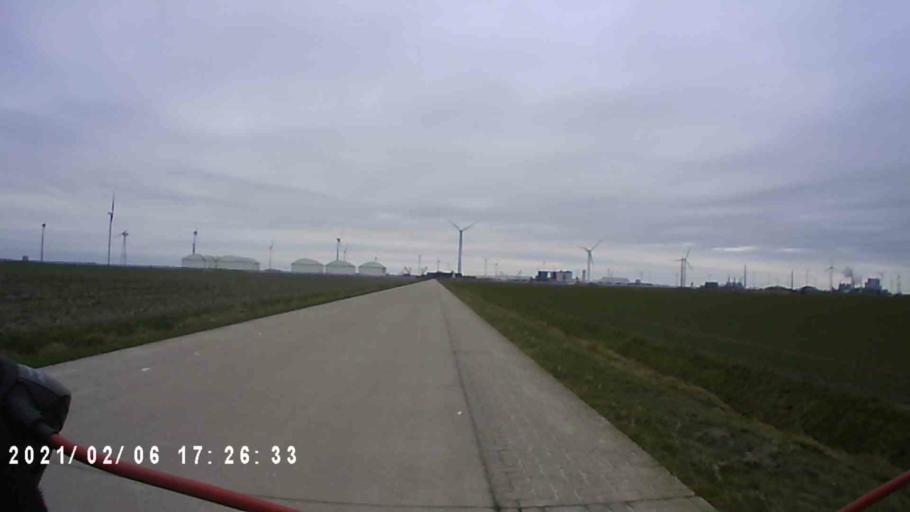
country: NL
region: Groningen
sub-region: Gemeente Appingedam
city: Appingedam
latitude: 53.4386
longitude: 6.7961
